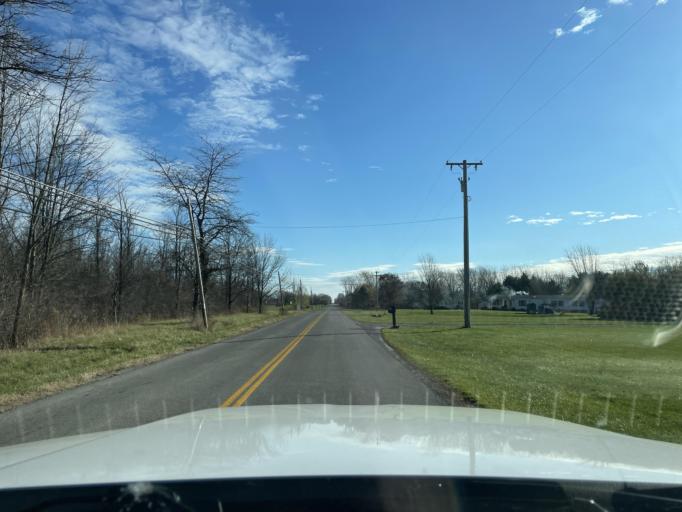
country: US
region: New York
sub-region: Niagara County
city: Gasport
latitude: 43.2068
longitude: -78.5376
